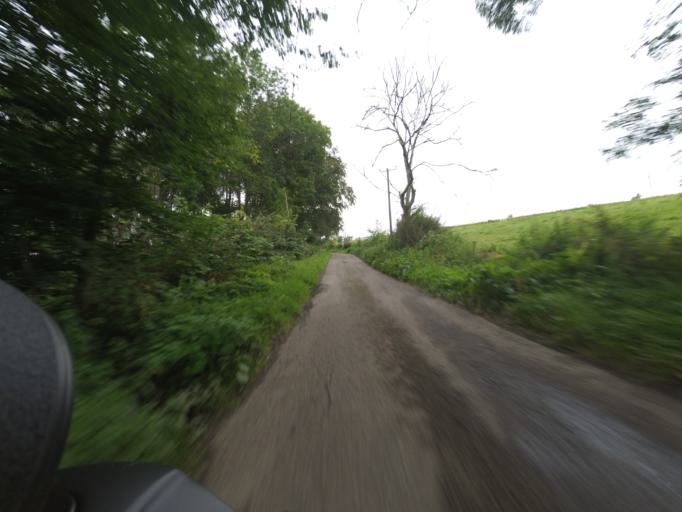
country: GB
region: Scotland
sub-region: Highland
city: Muir of Ord
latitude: 57.5126
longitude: -4.3899
